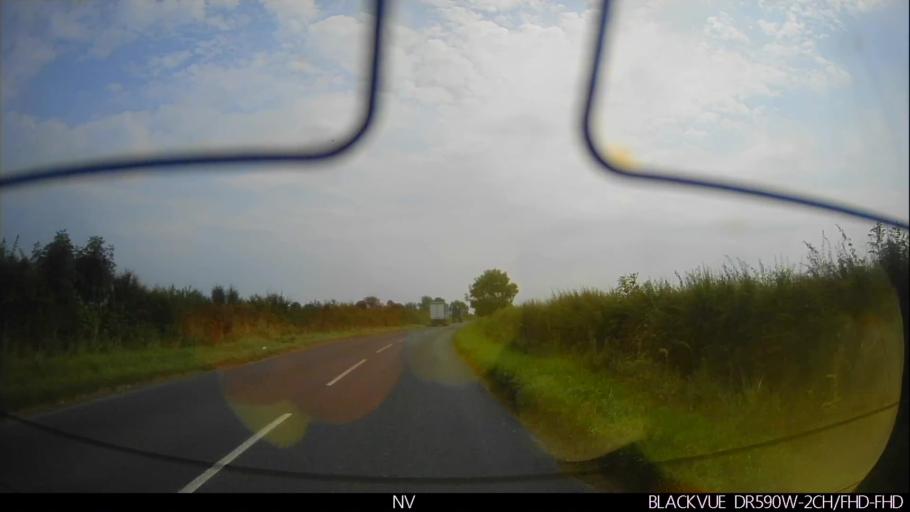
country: GB
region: England
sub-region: North Yorkshire
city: Marishes
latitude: 54.2101
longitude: -0.7801
